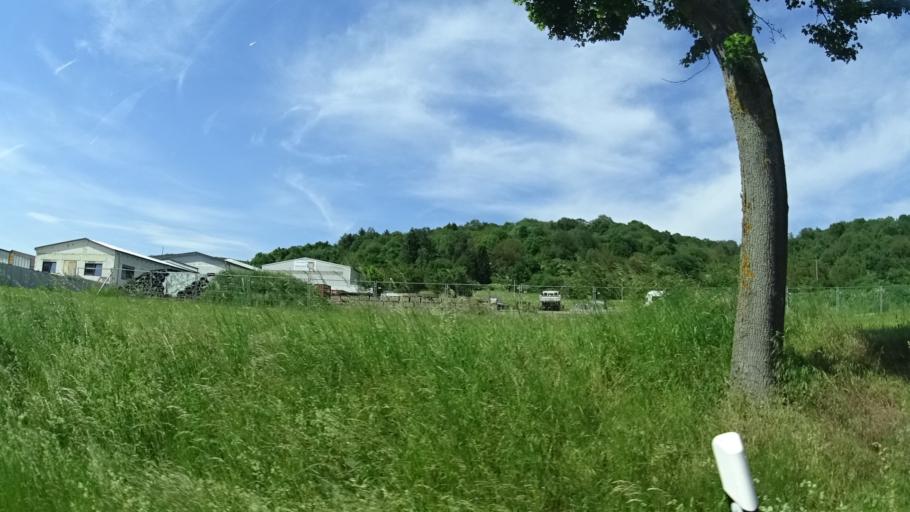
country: DE
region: Baden-Wuerttemberg
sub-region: Regierungsbezirk Stuttgart
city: Freudenberg
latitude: 49.7702
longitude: 9.3452
